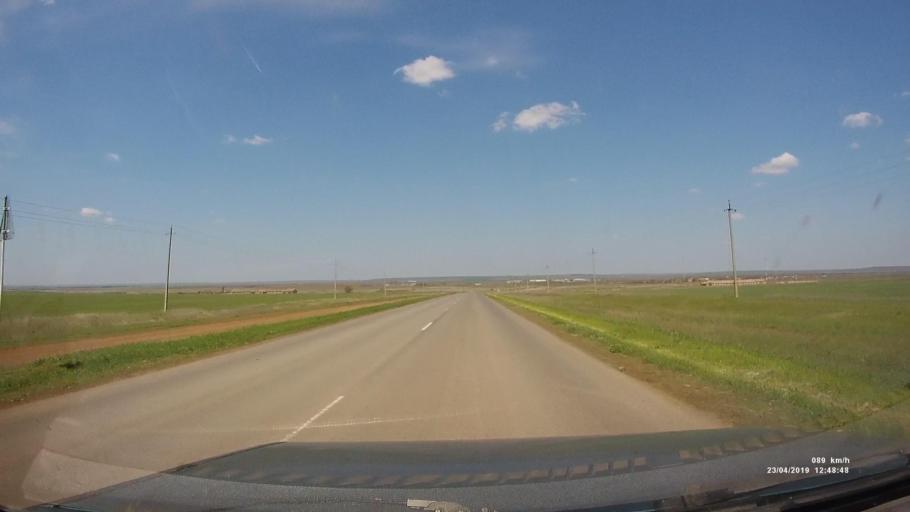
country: RU
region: Kalmykiya
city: Yashalta
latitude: 46.5291
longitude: 42.6390
